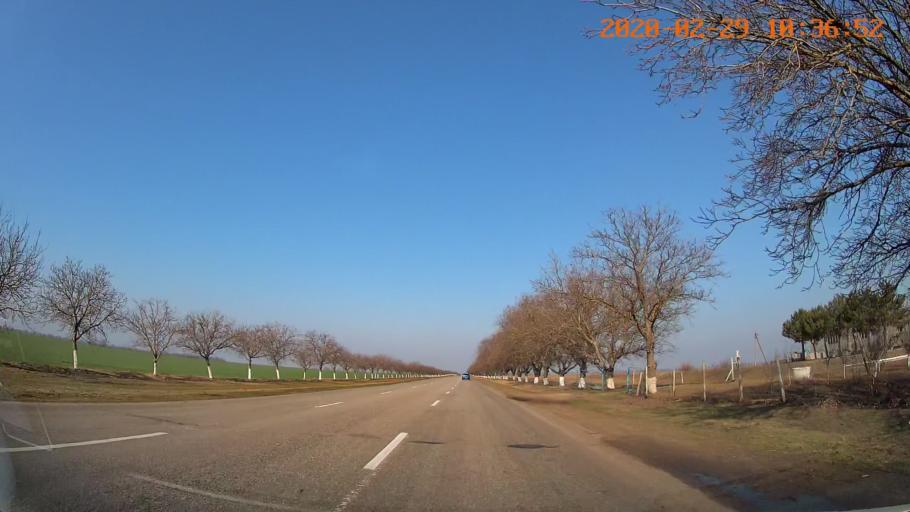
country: MD
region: Anenii Noi
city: Varnita
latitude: 47.0001
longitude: 29.4984
